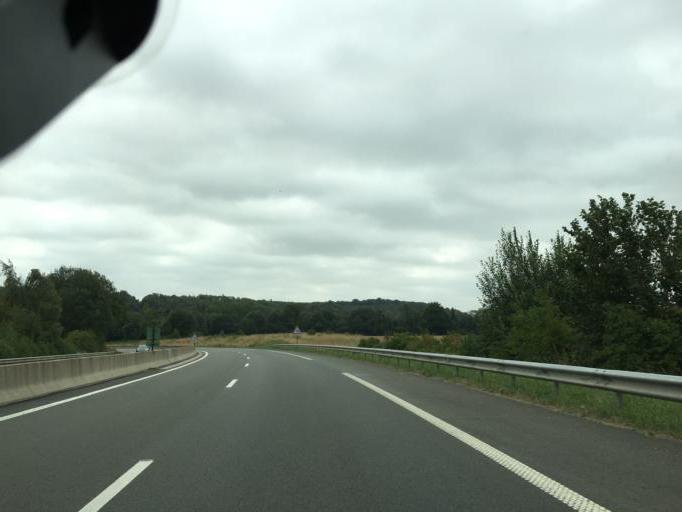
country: FR
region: Nord-Pas-de-Calais
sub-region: Departement du Pas-de-Calais
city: Saint-Pol-sur-Ternoise
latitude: 50.3687
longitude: 2.3027
